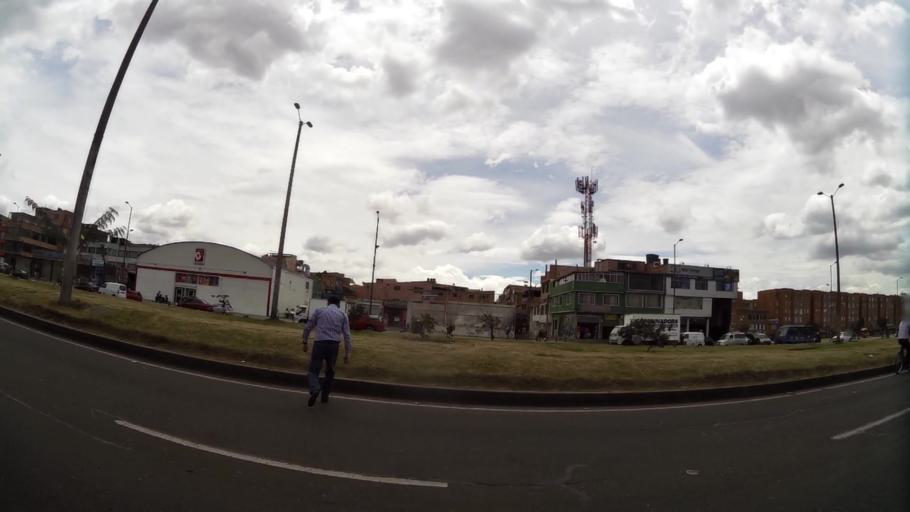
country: CO
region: Bogota D.C.
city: Bogota
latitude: 4.6379
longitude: -74.1547
